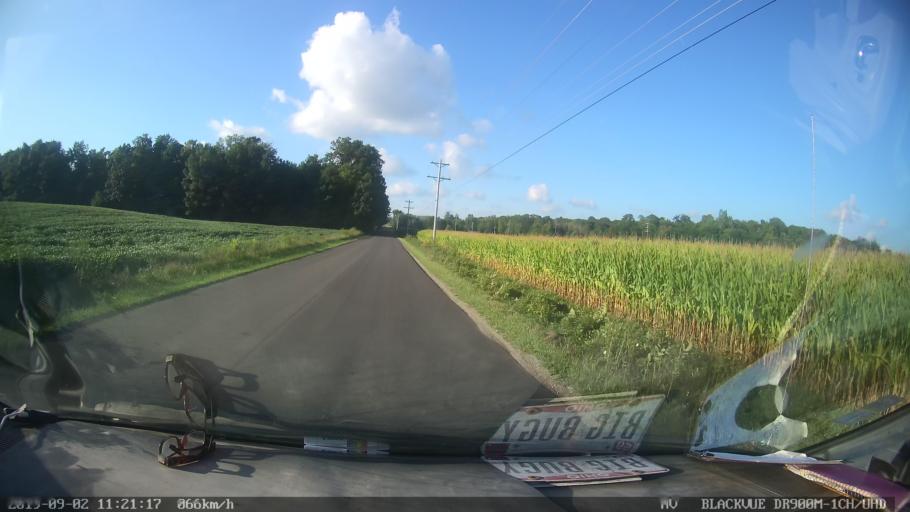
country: US
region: Ohio
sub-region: Morrow County
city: Mount Gilead
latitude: 40.5172
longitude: -82.7409
